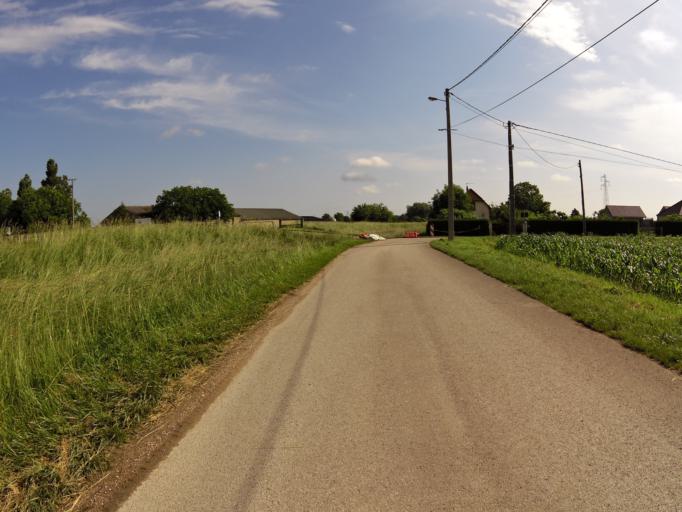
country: FR
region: Champagne-Ardenne
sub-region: Departement de l'Aube
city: Saint-Parres-aux-Tertres
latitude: 48.2689
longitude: 4.1396
